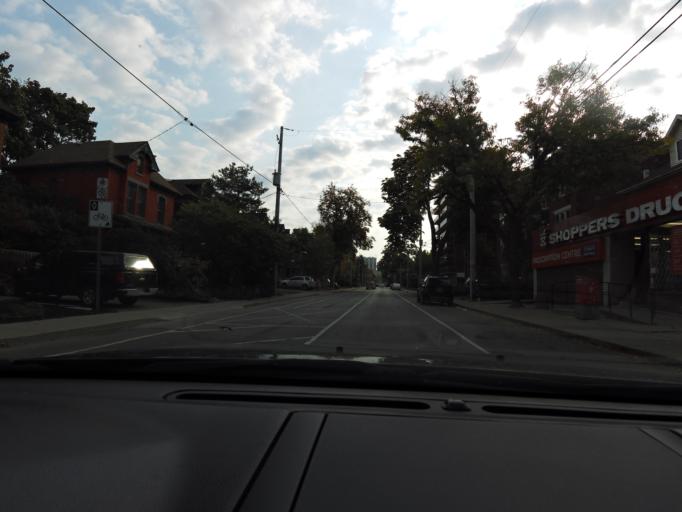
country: CA
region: Ontario
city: Hamilton
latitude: 43.2505
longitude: -79.8791
